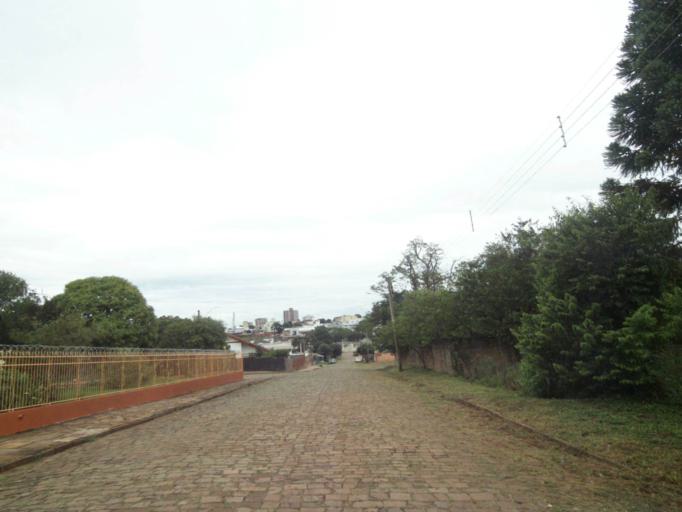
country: BR
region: Rio Grande do Sul
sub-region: Lagoa Vermelha
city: Lagoa Vermelha
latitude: -28.2165
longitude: -51.5200
